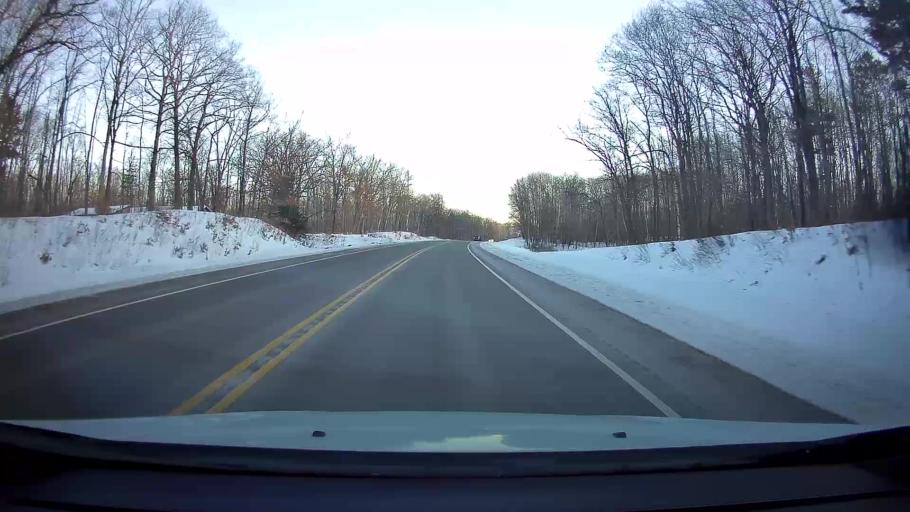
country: US
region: Wisconsin
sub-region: Washburn County
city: Shell Lake
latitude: 45.6725
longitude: -91.9931
